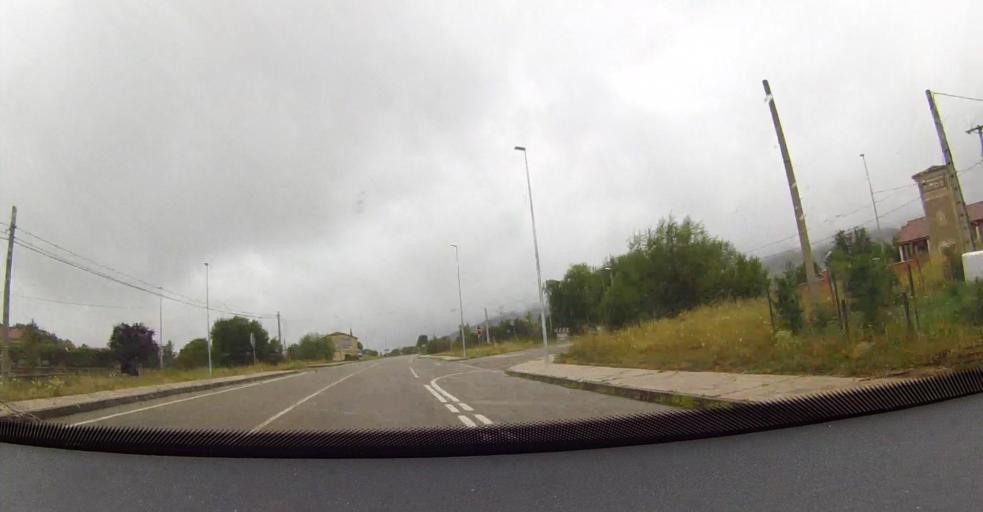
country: ES
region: Castille and Leon
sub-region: Provincia de Leon
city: Bonar
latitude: 42.8408
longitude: -5.2536
